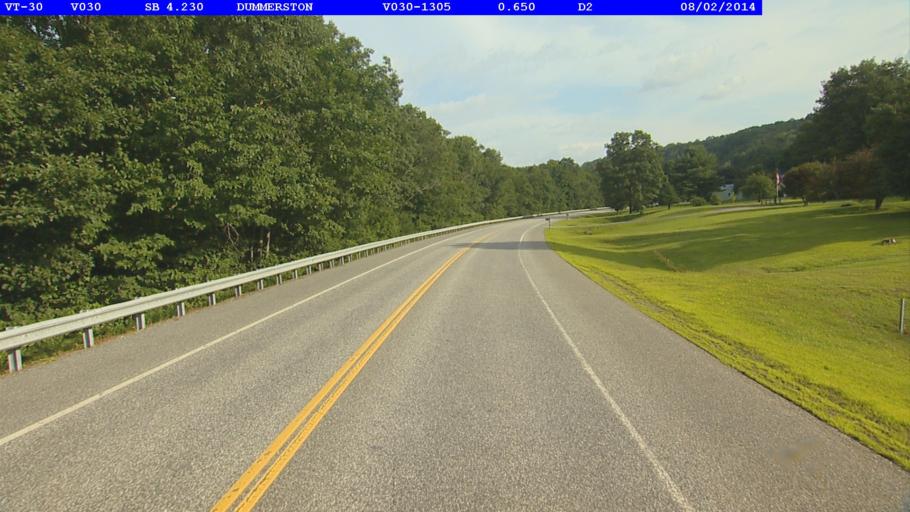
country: US
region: Vermont
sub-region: Windham County
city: West Brattleboro
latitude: 42.9062
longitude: -72.6014
